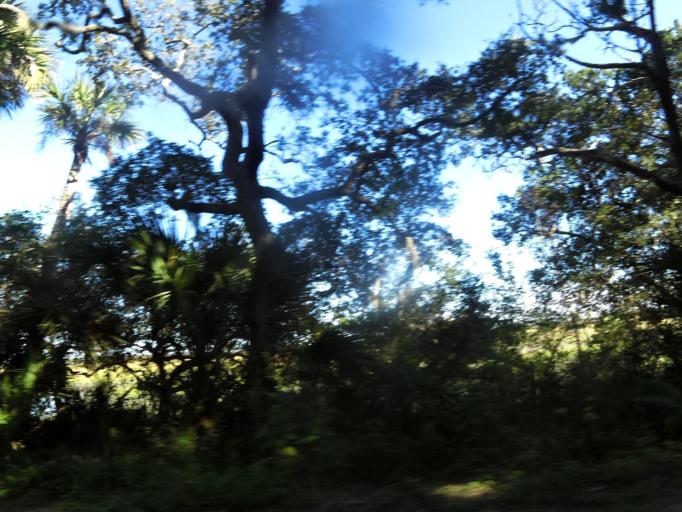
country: US
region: Florida
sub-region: Duval County
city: Atlantic Beach
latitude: 30.4176
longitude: -81.4273
